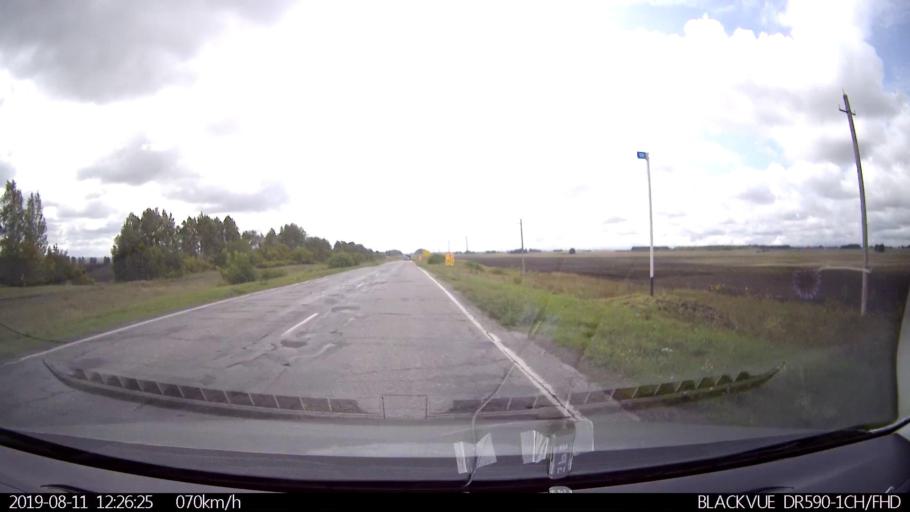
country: RU
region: Ulyanovsk
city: Ignatovka
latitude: 53.8642
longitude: 47.9306
